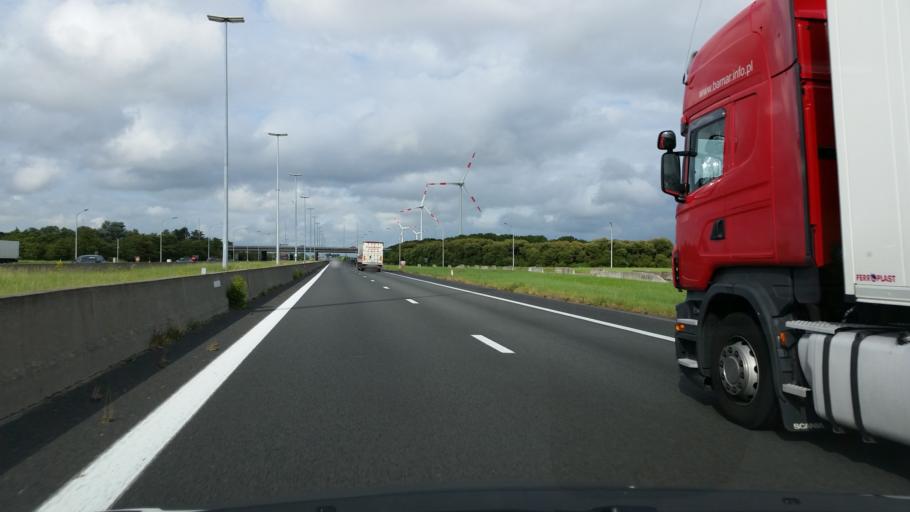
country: BE
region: Flanders
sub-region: Provincie West-Vlaanderen
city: Gistel
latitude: 51.1577
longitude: 2.9331
